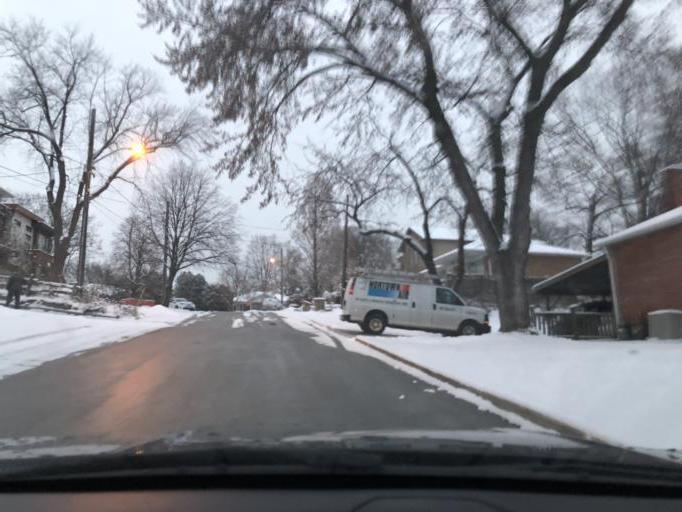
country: CA
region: Ontario
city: Toronto
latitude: 43.7024
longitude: -79.4861
